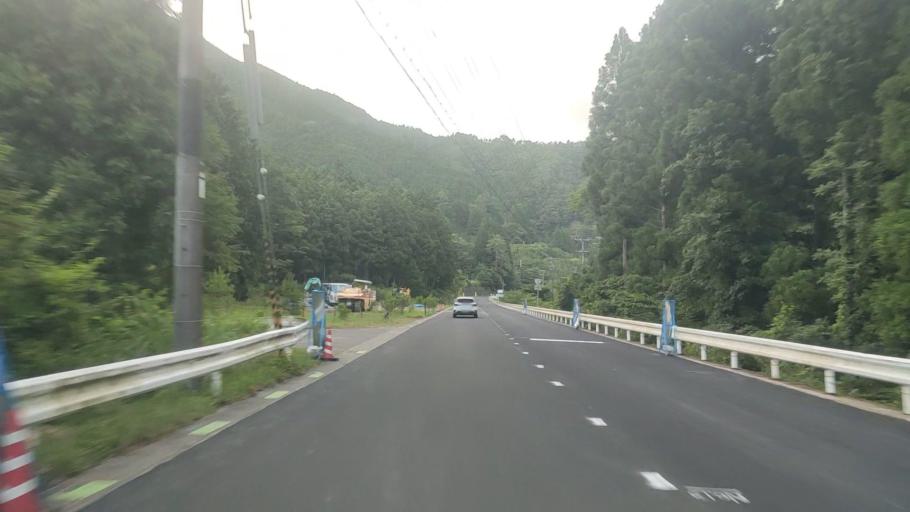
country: JP
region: Wakayama
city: Tanabe
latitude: 33.8325
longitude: 135.6520
